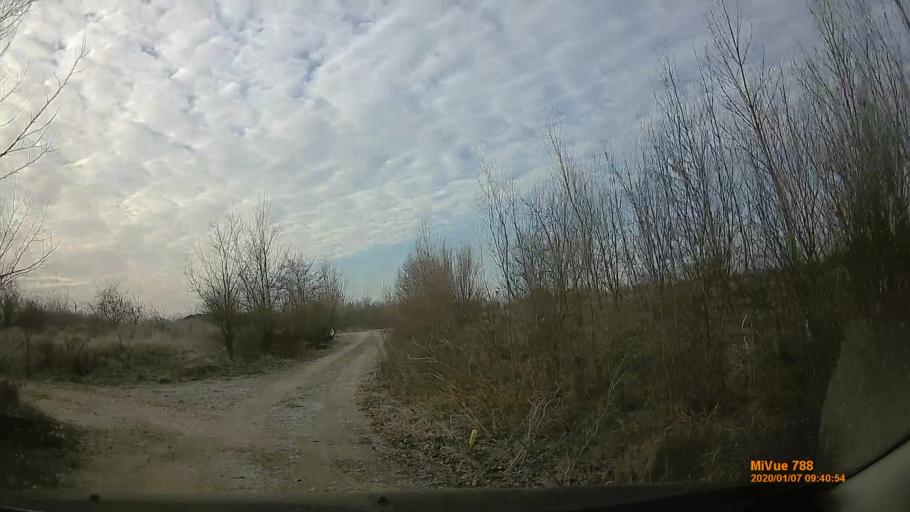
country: HU
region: Gyor-Moson-Sopron
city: Rajka
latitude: 47.9393
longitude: 17.1720
